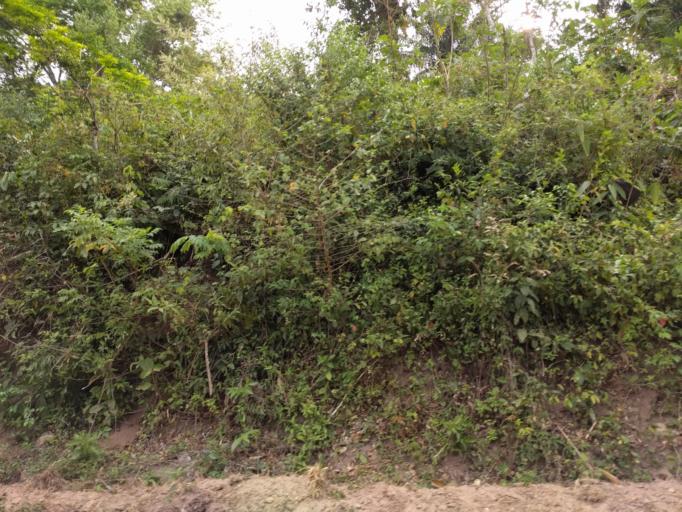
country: BO
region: Santa Cruz
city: Santiago del Torno
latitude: -17.9086
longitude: -63.4360
